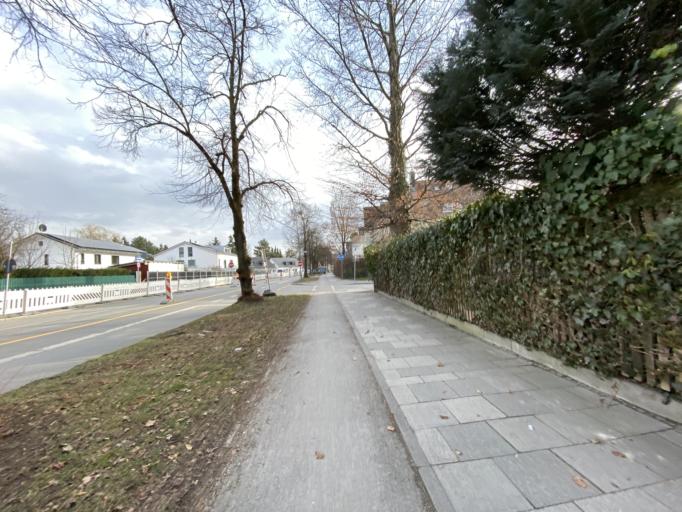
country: DE
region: Bavaria
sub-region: Upper Bavaria
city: Bogenhausen
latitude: 48.1439
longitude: 11.6276
